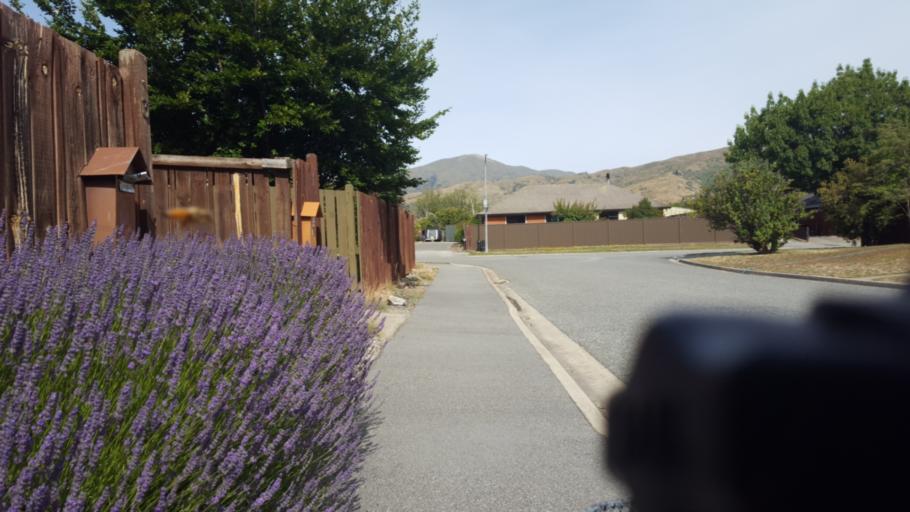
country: NZ
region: Otago
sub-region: Queenstown-Lakes District
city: Wanaka
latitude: -45.0410
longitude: 169.1895
